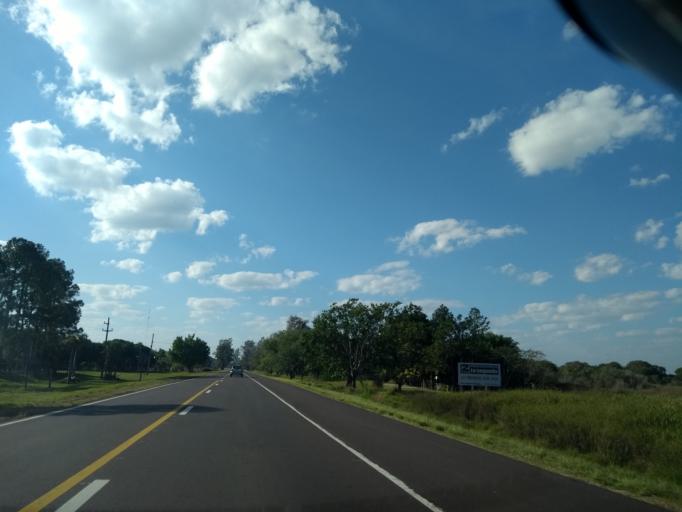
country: AR
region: Corrientes
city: Paso de la Patria
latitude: -27.3906
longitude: -58.5865
